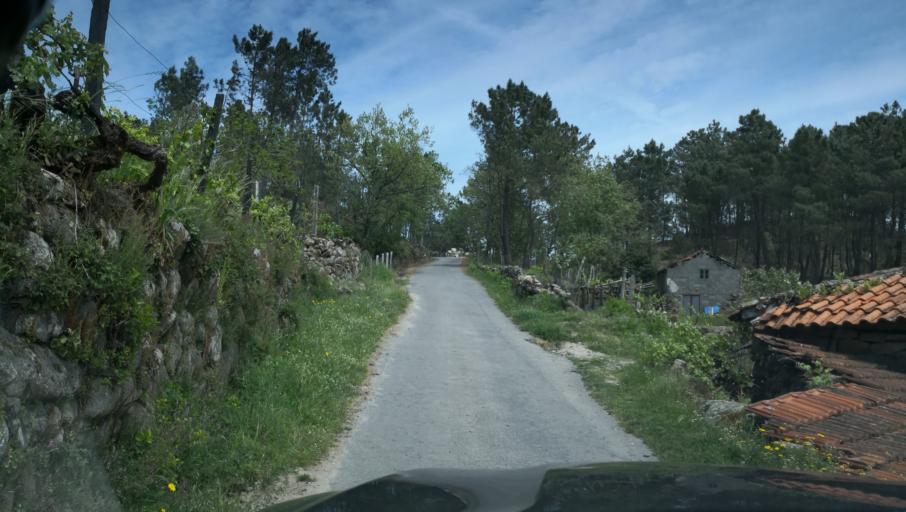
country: PT
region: Vila Real
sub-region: Vila Real
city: Vila Real
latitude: 41.3064
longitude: -7.8016
